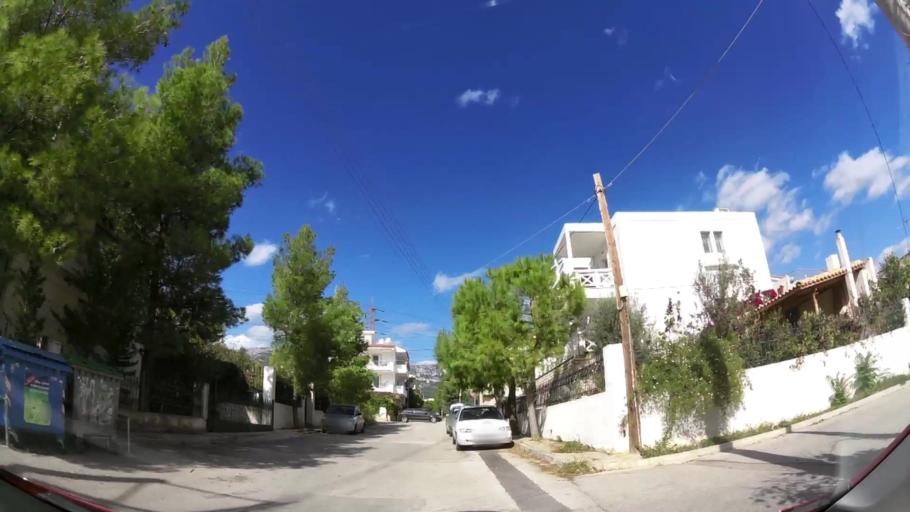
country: GR
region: Attica
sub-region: Nomarchia Anatolikis Attikis
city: Acharnes
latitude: 38.1020
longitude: 23.7388
